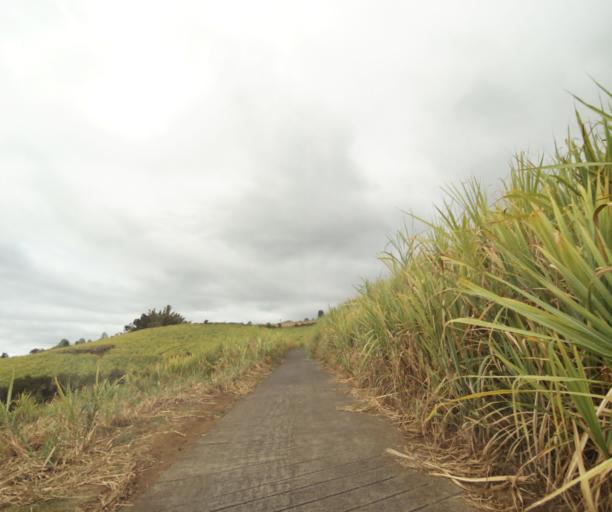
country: RE
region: Reunion
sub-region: Reunion
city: Saint-Paul
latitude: -21.0261
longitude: 55.3208
